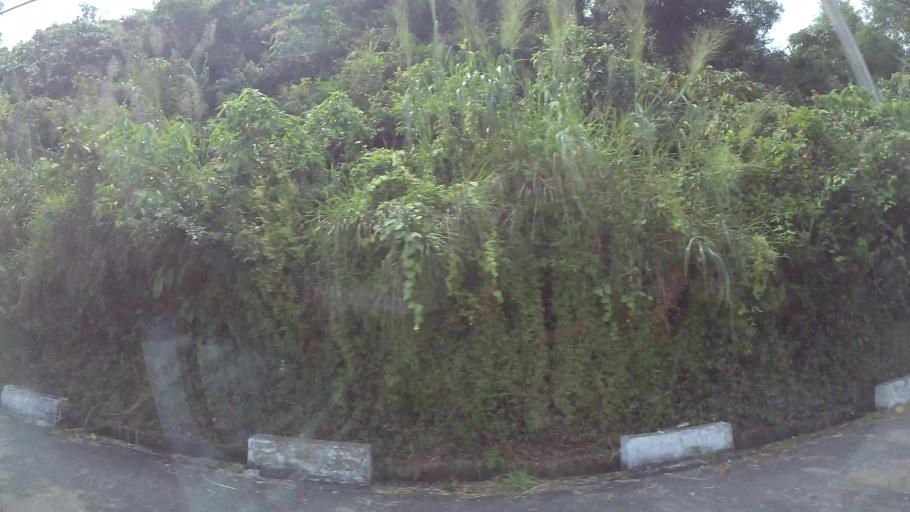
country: VN
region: Da Nang
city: Son Tra
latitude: 16.1016
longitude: 108.2808
